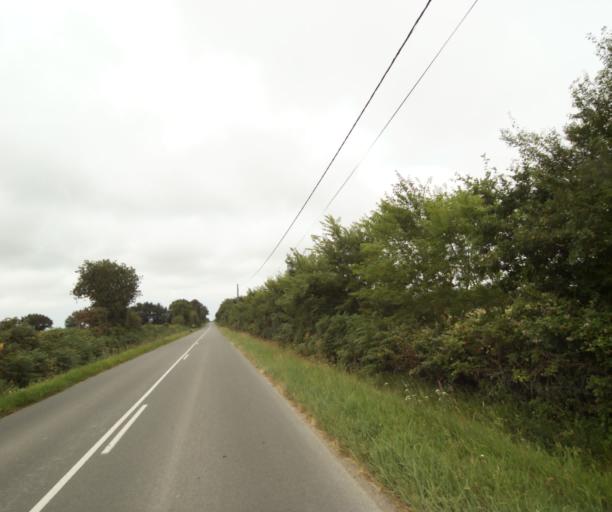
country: FR
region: Pays de la Loire
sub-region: Departement de la Vendee
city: Sainte-Foy
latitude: 46.5087
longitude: -1.6868
